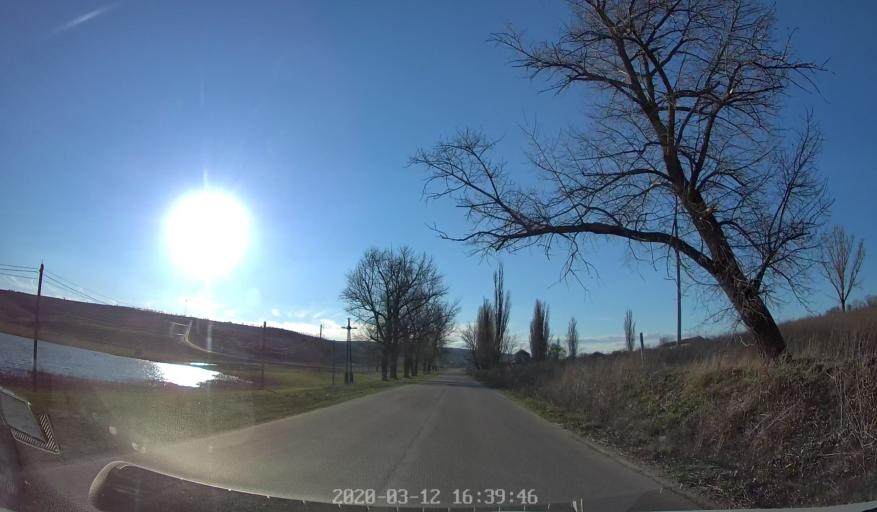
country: MD
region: Anenii Noi
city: Anenii Noi
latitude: 46.8159
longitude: 29.1596
